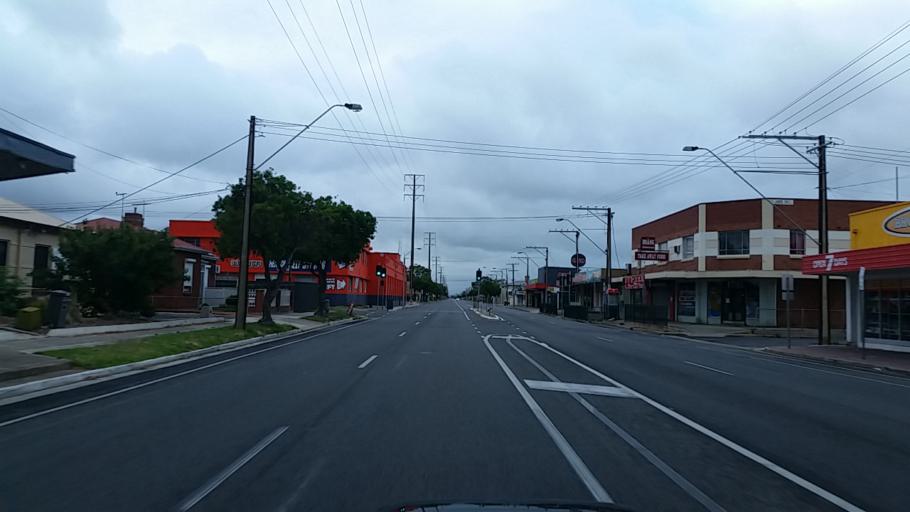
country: AU
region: South Australia
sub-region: Port Adelaide Enfield
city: Cheltenham
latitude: -34.8689
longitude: 138.5121
